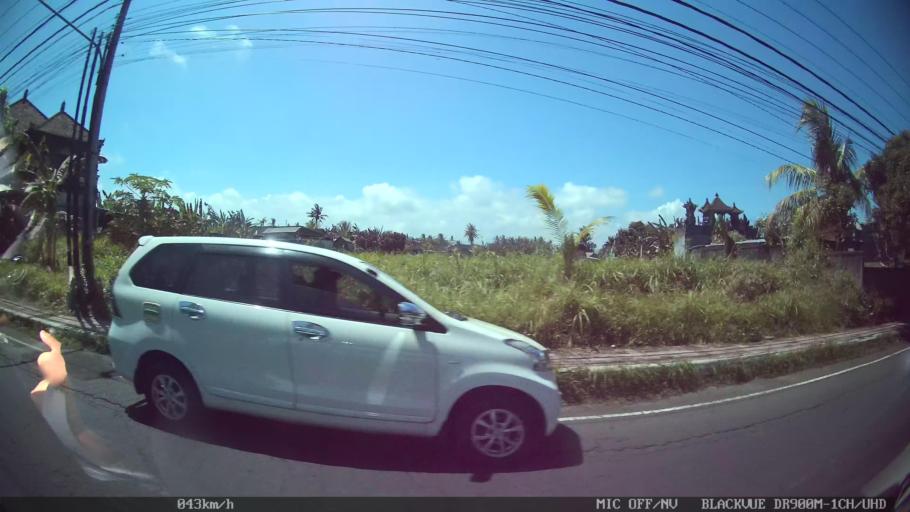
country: ID
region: Bali
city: Klungkung
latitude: -8.5661
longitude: 115.3440
